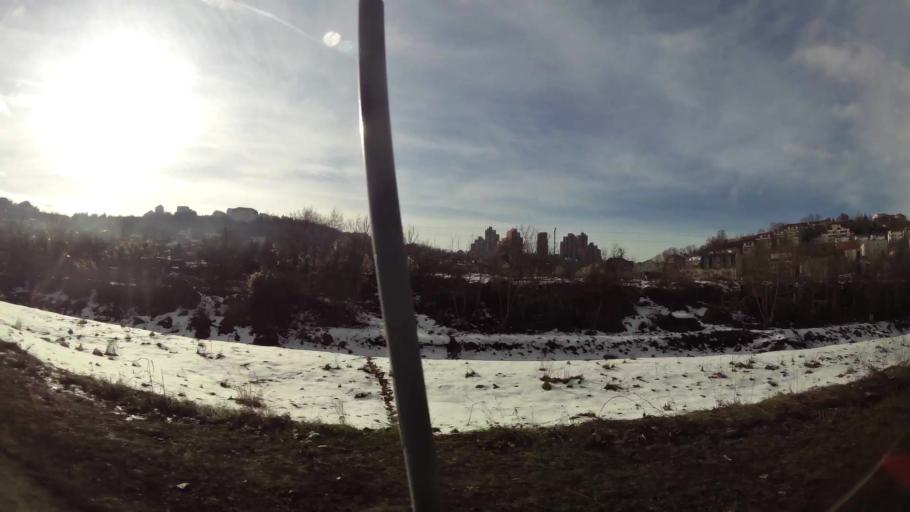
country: RS
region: Central Serbia
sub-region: Belgrade
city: Rakovica
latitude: 44.7337
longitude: 20.4315
